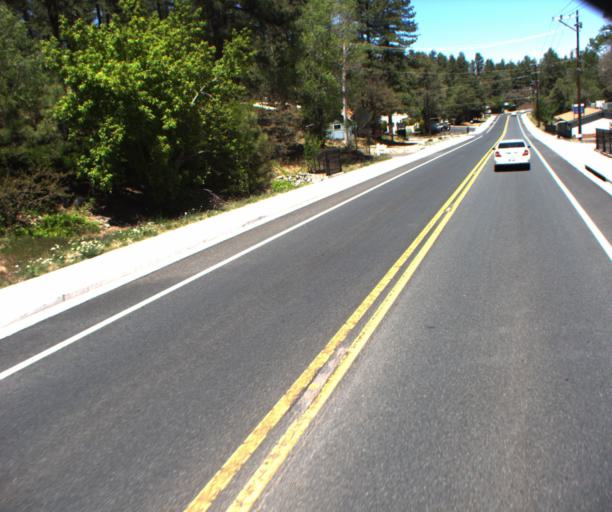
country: US
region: Arizona
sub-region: Yavapai County
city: Prescott
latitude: 34.5208
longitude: -112.4794
